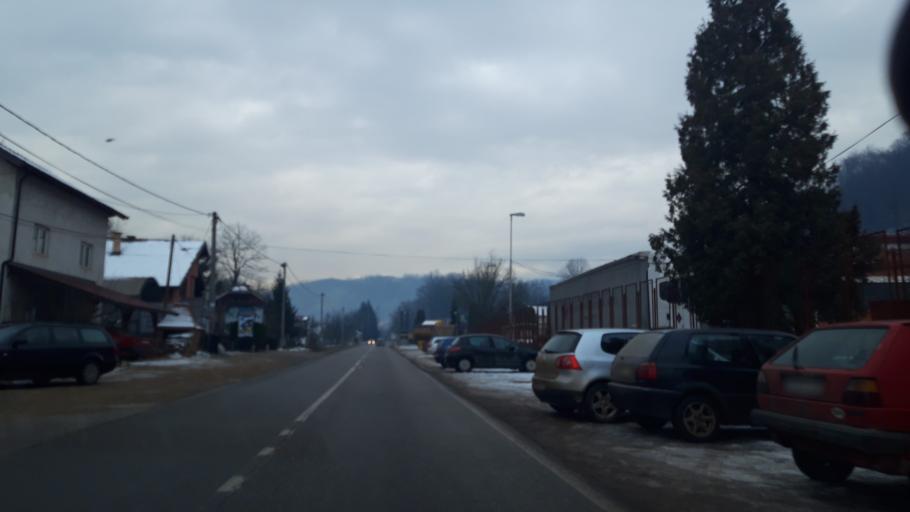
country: BA
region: Republika Srpska
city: Milici
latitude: 44.1756
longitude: 19.0748
